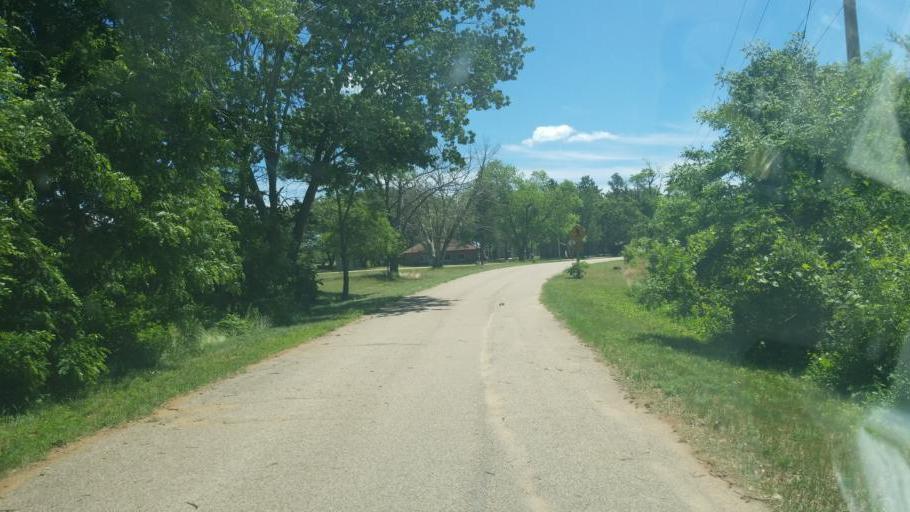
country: US
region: Wisconsin
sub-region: Juneau County
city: New Lisbon
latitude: 44.0218
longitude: -90.0591
